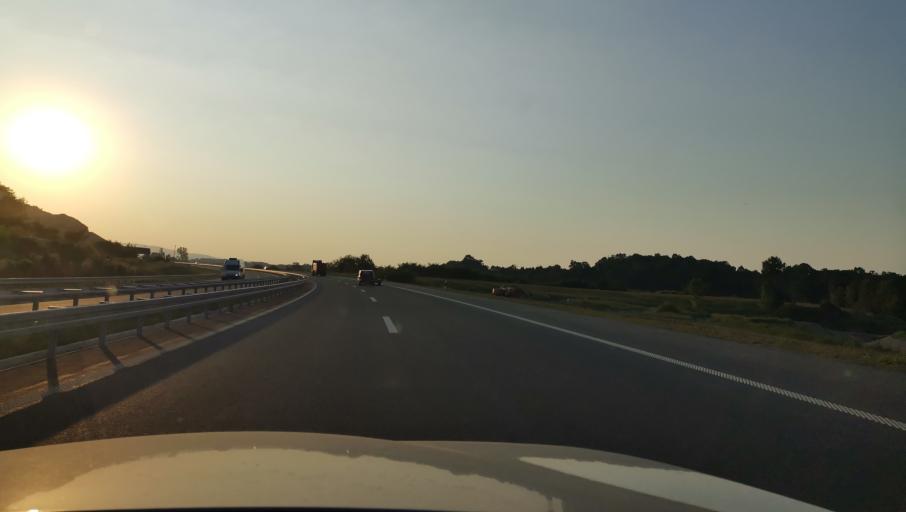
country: RS
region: Central Serbia
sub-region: Kolubarski Okrug
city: Lajkovac
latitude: 44.3425
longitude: 20.1936
